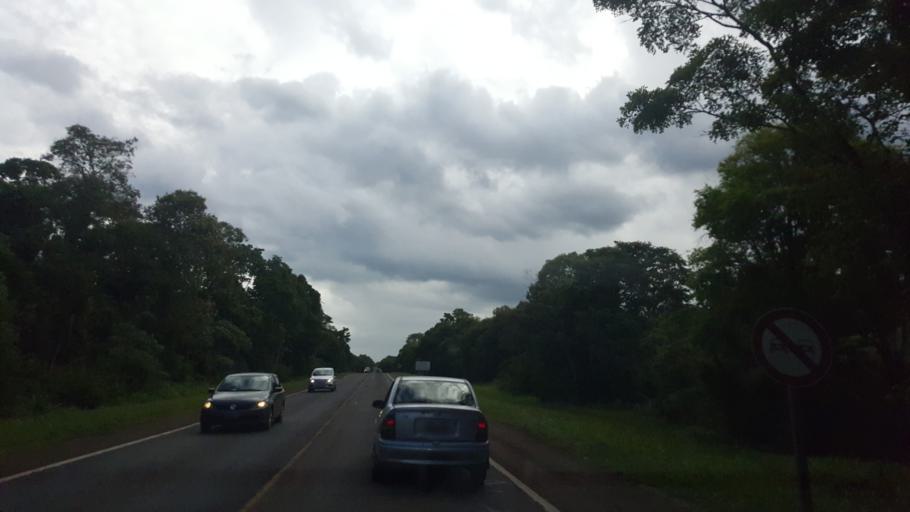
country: AR
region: Misiones
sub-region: Departamento de Iguazu
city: Puerto Iguazu
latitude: -25.7190
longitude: -54.5216
